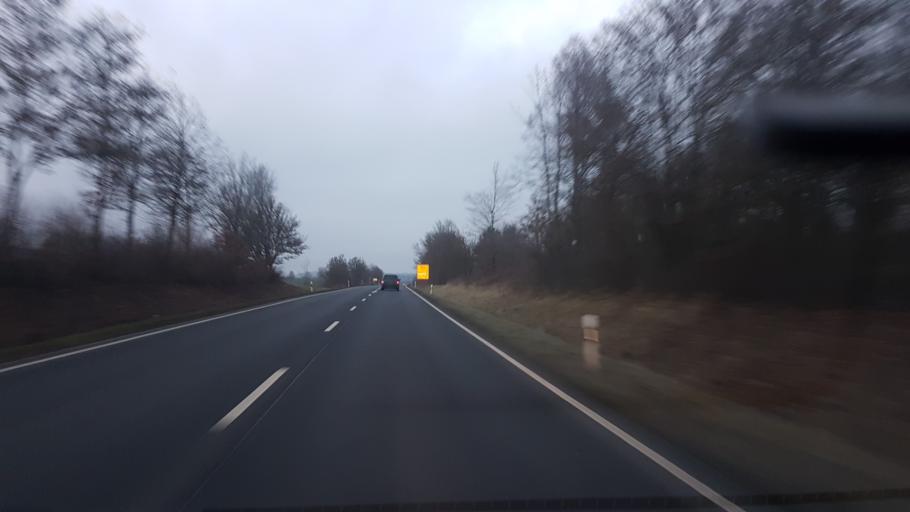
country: DE
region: Bavaria
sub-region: Regierungsbezirk Unterfranken
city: Pfarrweisach
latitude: 50.1227
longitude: 10.7620
